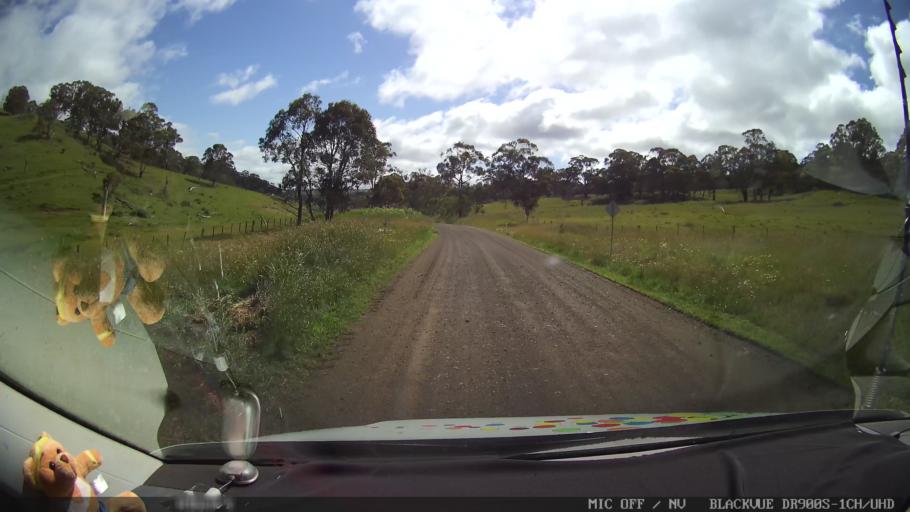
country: AU
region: New South Wales
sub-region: Guyra
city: Guyra
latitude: -29.9988
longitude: 151.6755
